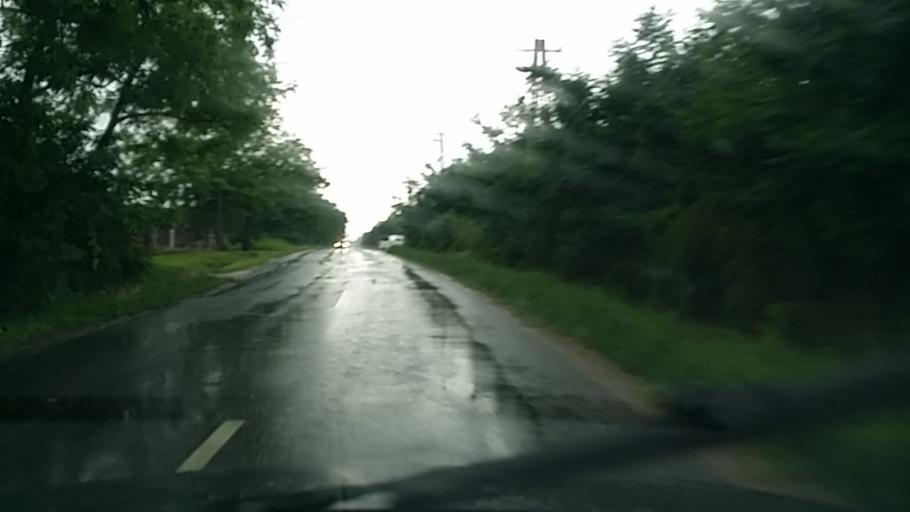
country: HU
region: Pest
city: Ocsa
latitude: 47.2919
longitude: 19.2512
